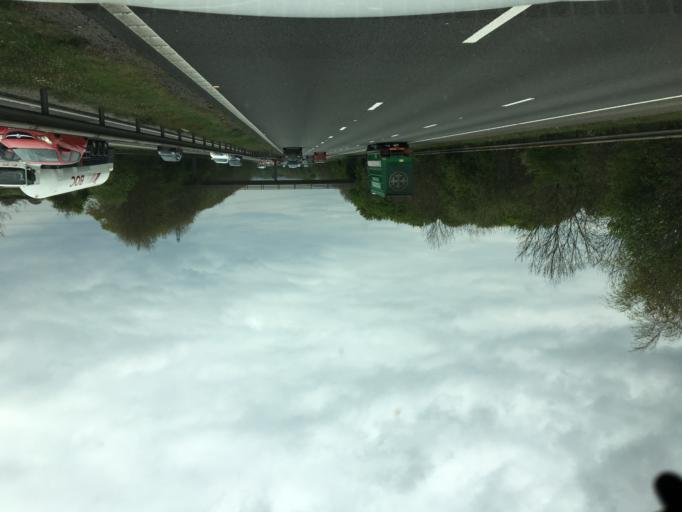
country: GB
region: Wales
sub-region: Rhondda Cynon Taf
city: Llanharry
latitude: 51.5135
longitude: -3.4138
